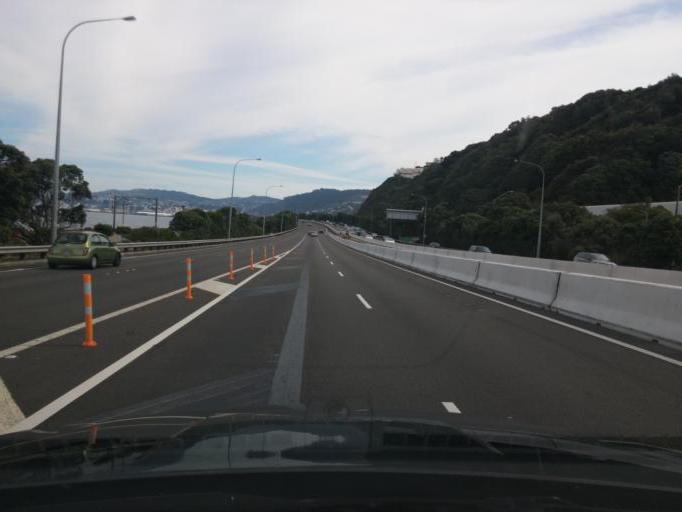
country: NZ
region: Wellington
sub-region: Wellington City
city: Wellington
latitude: -41.2494
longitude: 174.8112
